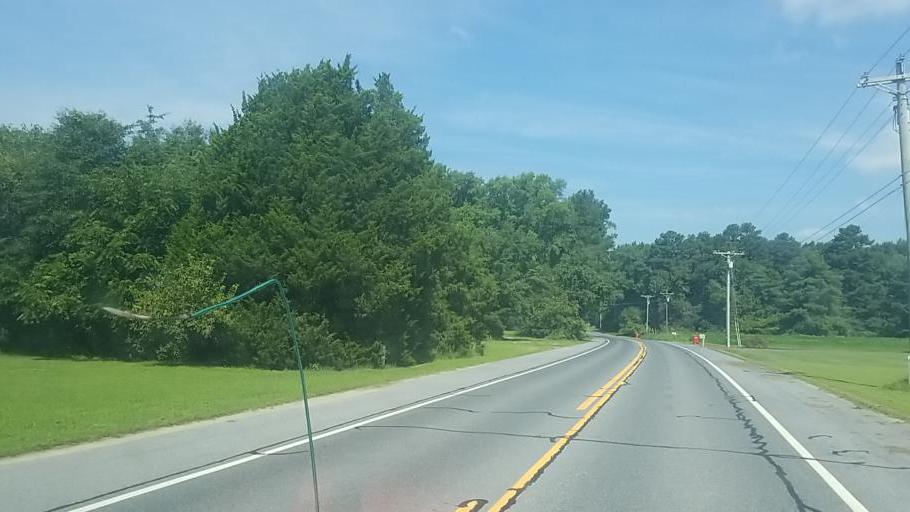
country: US
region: Delaware
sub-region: Sussex County
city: Seaford
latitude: 38.6742
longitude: -75.5758
